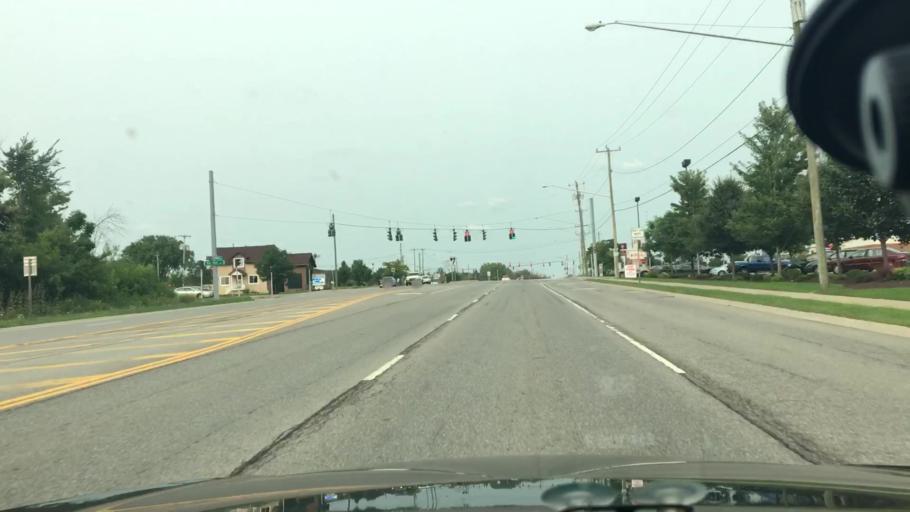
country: US
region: New York
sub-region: Erie County
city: Blasdell
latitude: 42.7685
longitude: -78.8145
